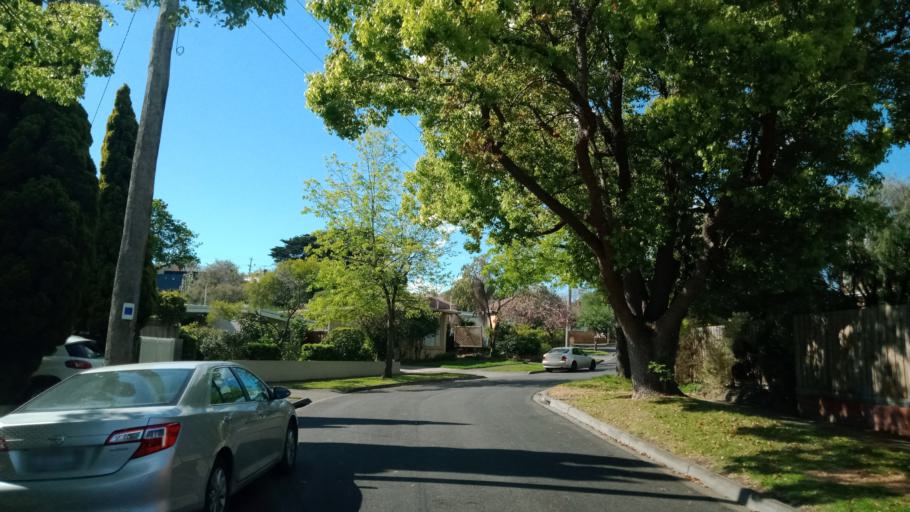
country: AU
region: Victoria
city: Glenferrie
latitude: -37.8468
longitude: 145.0510
